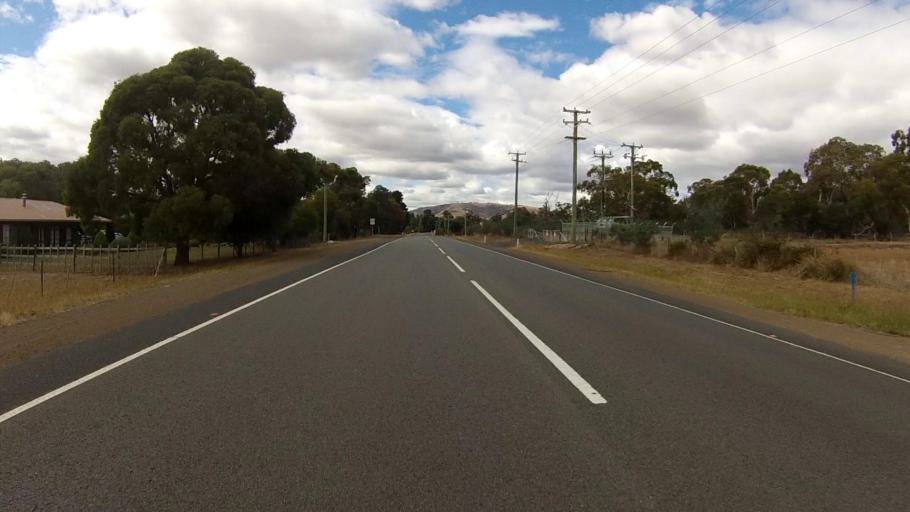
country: AU
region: Tasmania
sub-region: Brighton
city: Bridgewater
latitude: -42.6743
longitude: 147.2604
